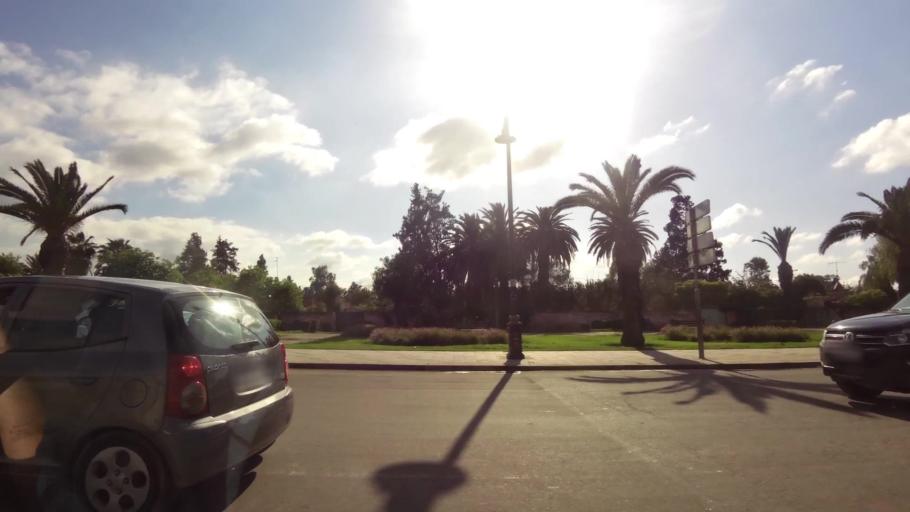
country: MA
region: Chaouia-Ouardigha
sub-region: Settat Province
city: Berrechid
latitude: 33.2620
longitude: -7.5818
